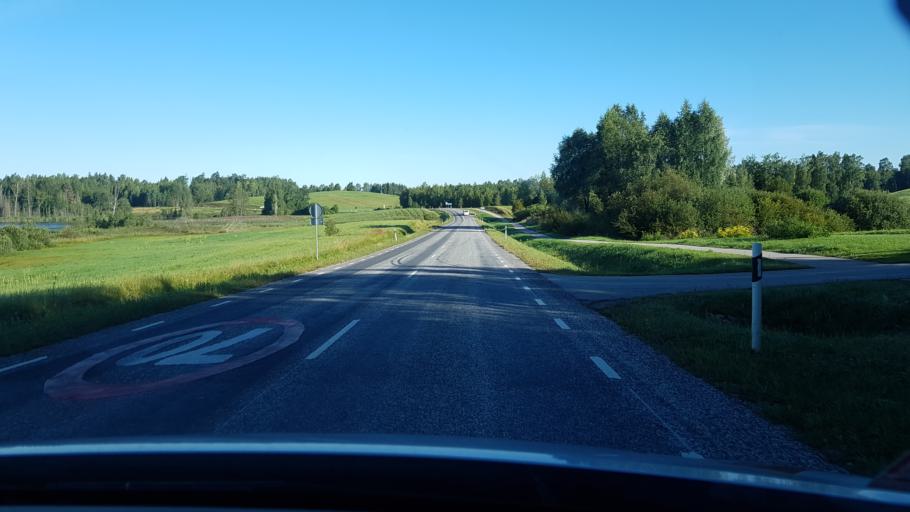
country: EE
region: Vorumaa
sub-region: Antsla vald
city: Vana-Antsla
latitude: 58.0535
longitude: 26.5358
